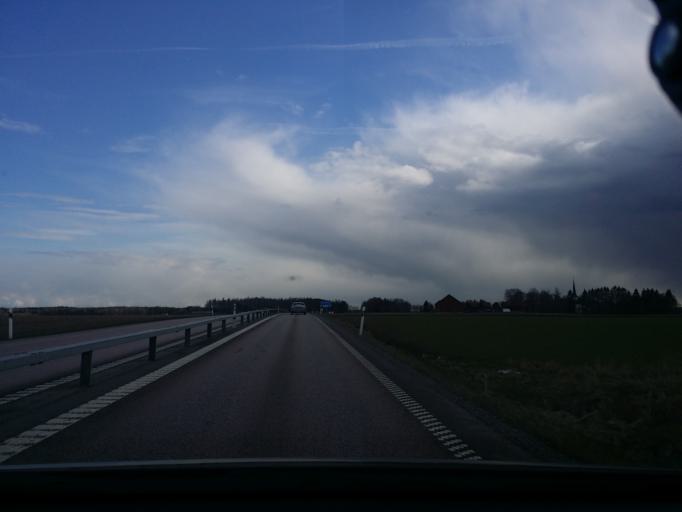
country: SE
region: Vaestmanland
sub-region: Vasteras
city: Hokasen
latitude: 59.7411
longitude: 16.5602
